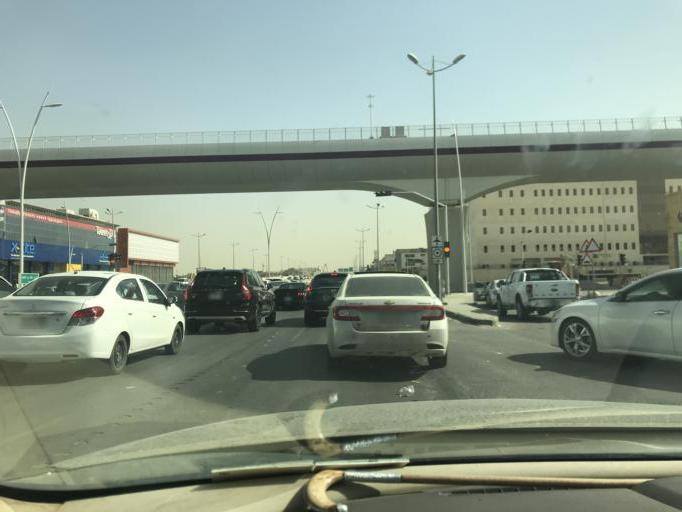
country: SA
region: Ar Riyad
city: Riyadh
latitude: 24.7932
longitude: 46.7437
